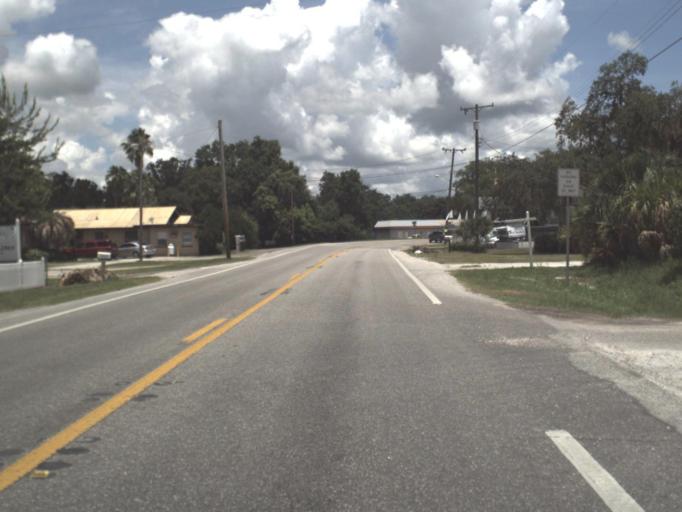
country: US
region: Florida
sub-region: Hillsborough County
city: Plant City
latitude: 28.0129
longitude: -82.1547
